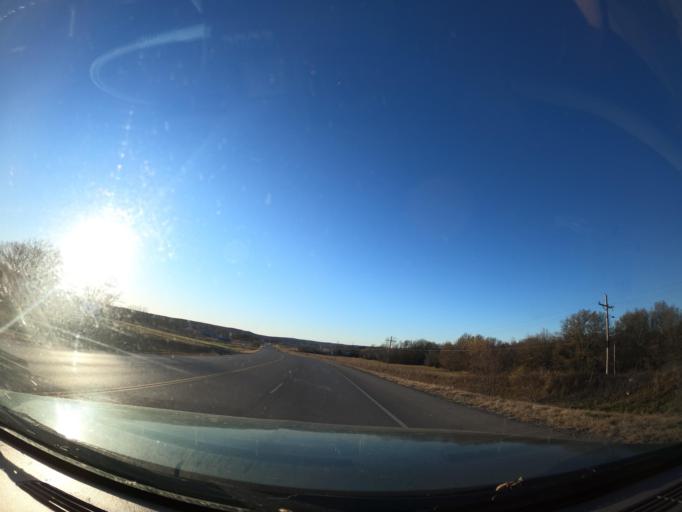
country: US
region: Oklahoma
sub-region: Pittsburg County
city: Krebs
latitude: 34.8949
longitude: -95.6531
